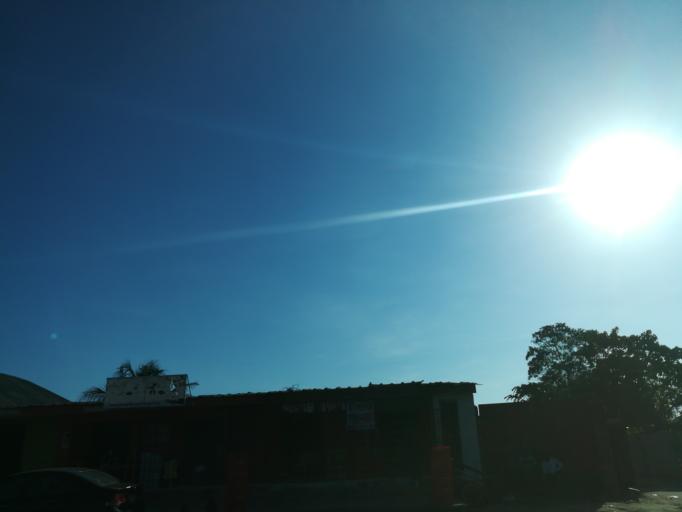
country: NG
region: Lagos
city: Ebute Ikorodu
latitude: 6.5499
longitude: 3.5411
